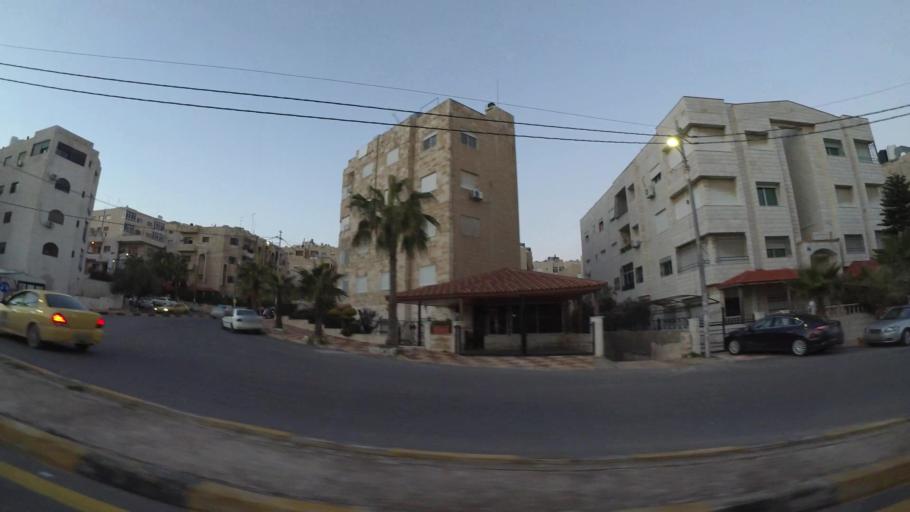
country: JO
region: Amman
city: Al Jubayhah
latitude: 31.9878
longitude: 35.8849
